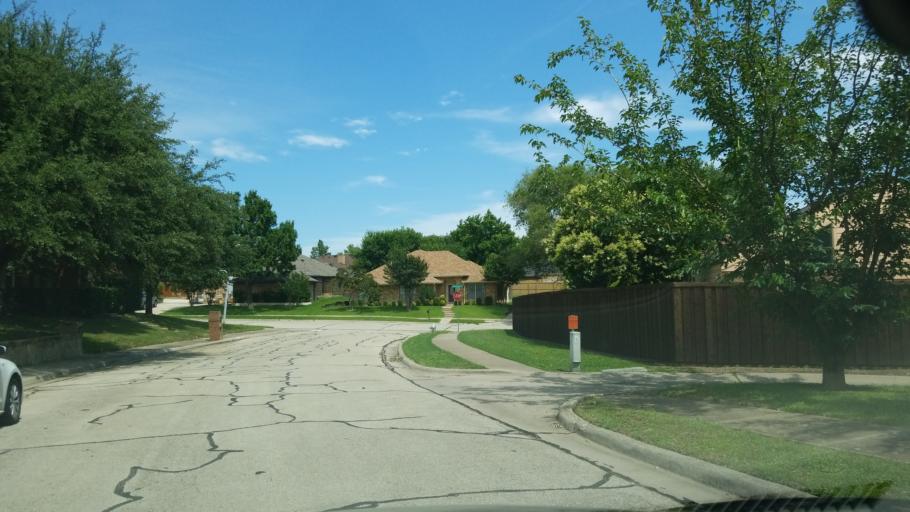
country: US
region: Texas
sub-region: Dallas County
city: Irving
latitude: 32.8757
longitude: -96.9990
